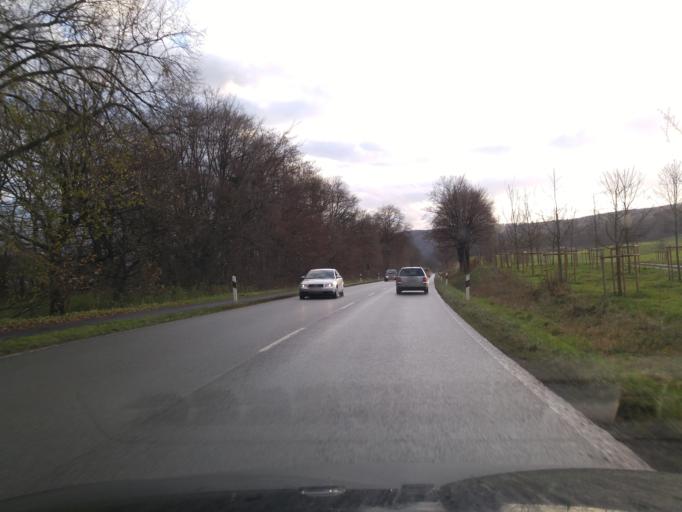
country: DE
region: Lower Saxony
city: Hannoversch Munden
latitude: 51.4466
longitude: 9.6387
